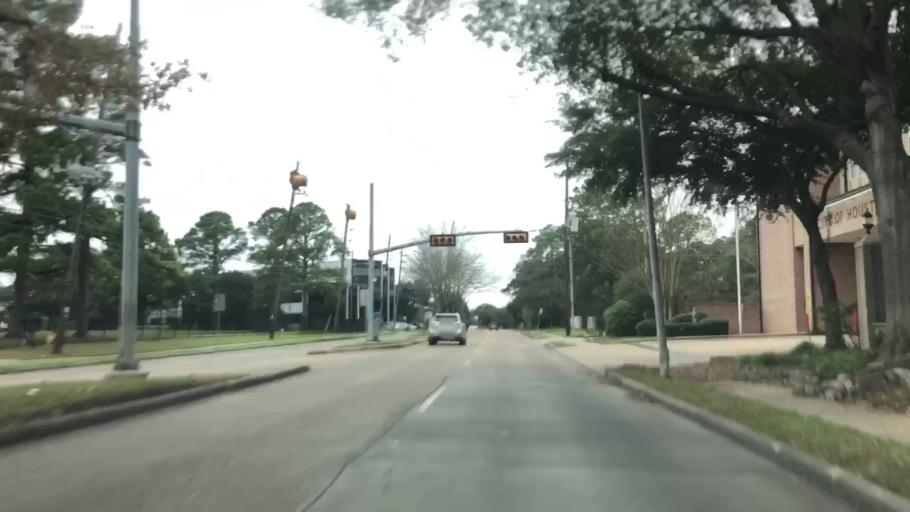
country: US
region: Texas
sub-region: Harris County
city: Hunters Creek Village
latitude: 29.7625
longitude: -95.4805
